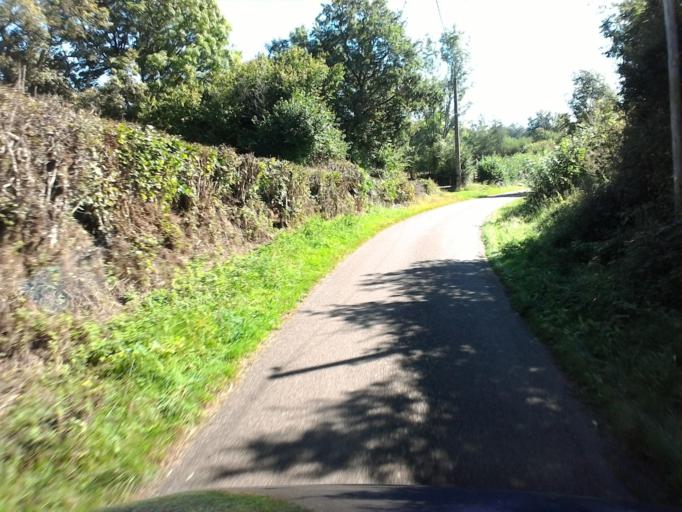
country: FR
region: Bourgogne
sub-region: Departement de la Cote-d'Or
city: Saulieu
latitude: 47.2518
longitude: 4.2155
